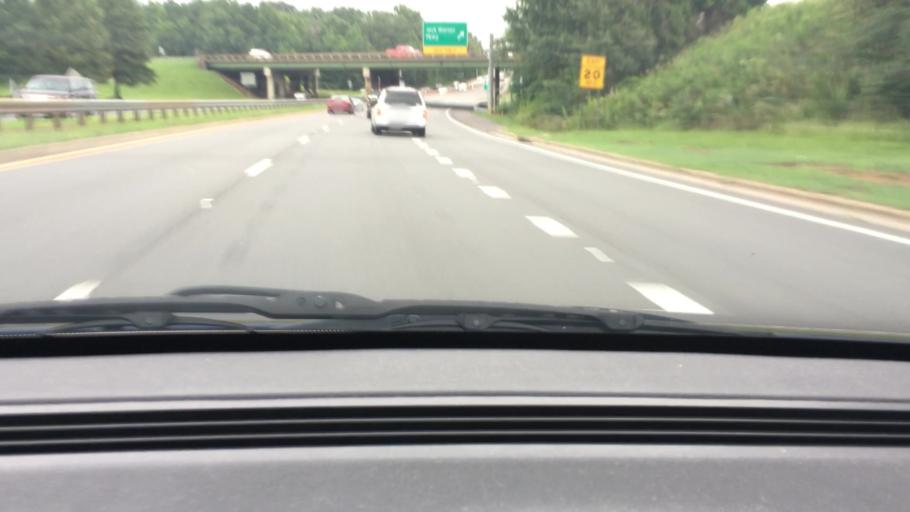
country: US
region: Alabama
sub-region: Tuscaloosa County
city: Tuscaloosa
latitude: 33.2187
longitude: -87.5311
